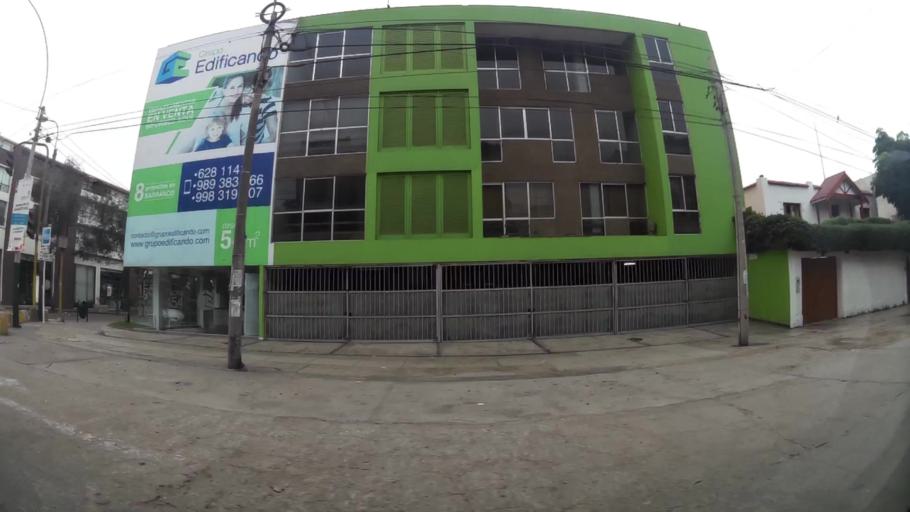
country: PE
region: Lima
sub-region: Lima
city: Surco
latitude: -12.1413
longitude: -77.0235
